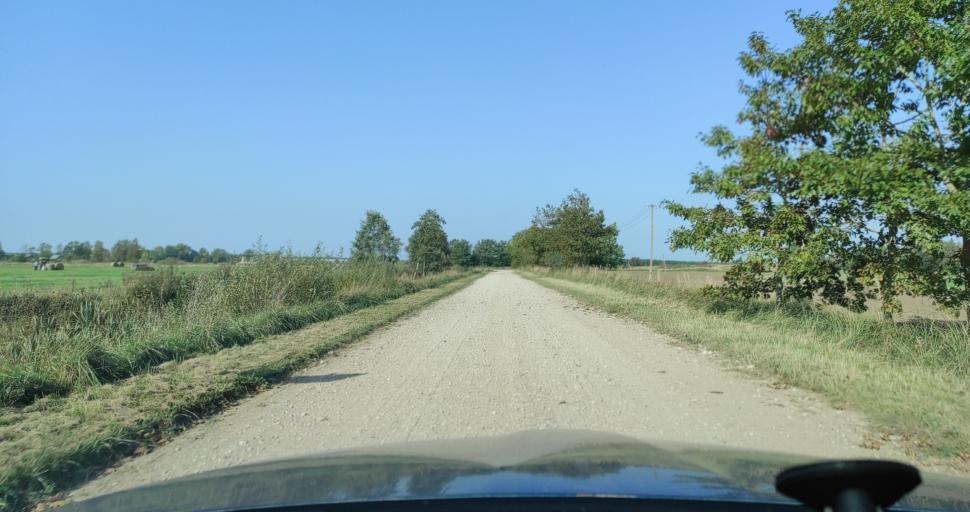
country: LV
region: Ventspils Rajons
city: Piltene
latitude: 57.2316
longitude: 21.6124
